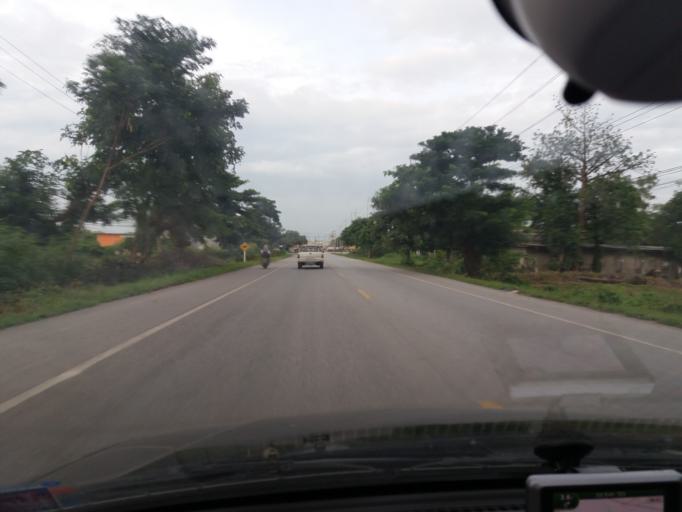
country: TH
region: Suphan Buri
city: U Thong
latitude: 14.4093
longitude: 99.8998
